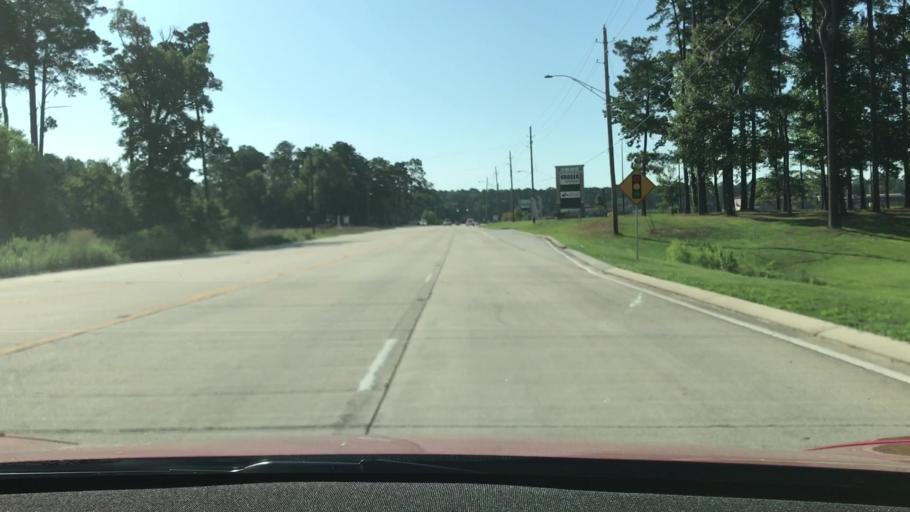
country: US
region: Louisiana
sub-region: Bossier Parish
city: Bossier City
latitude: 32.3979
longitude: -93.7306
